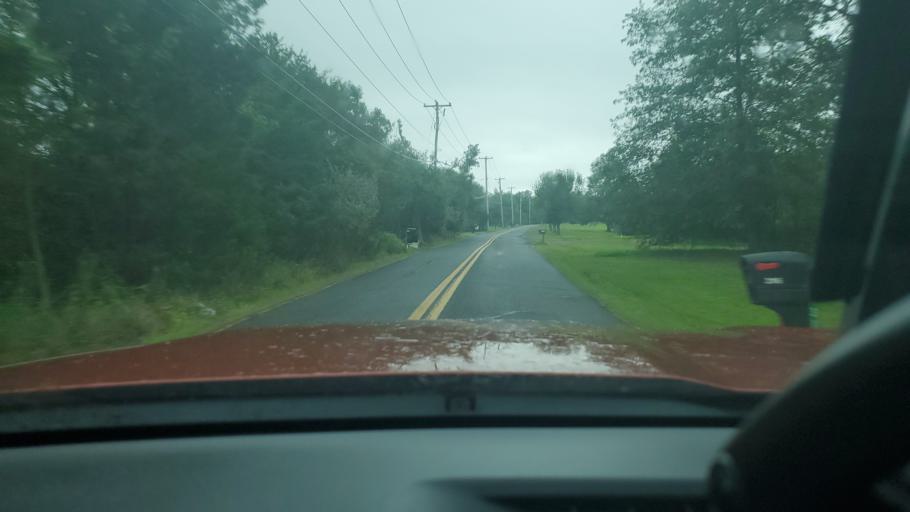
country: US
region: Pennsylvania
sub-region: Montgomery County
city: Spring Mount
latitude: 40.3051
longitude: -75.5072
